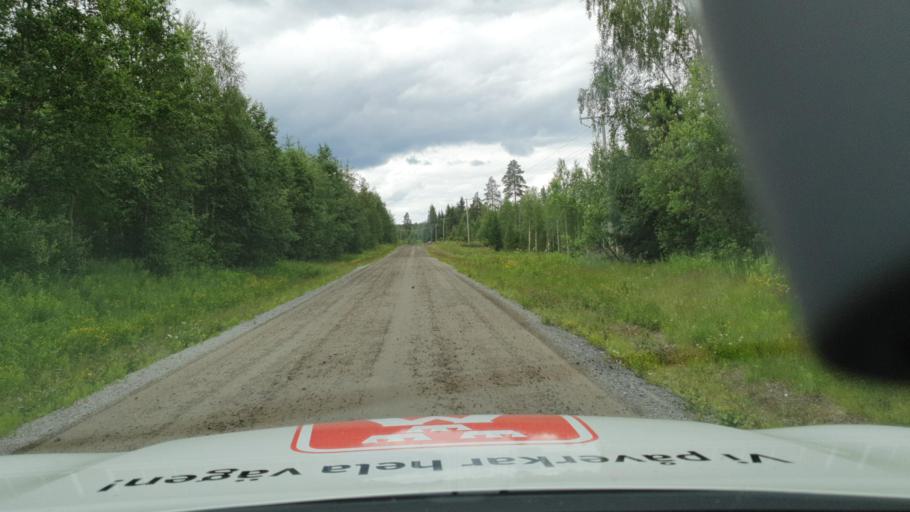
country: SE
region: Vaesterbotten
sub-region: Bjurholms Kommun
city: Bjurholm
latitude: 63.8035
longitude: 19.0803
